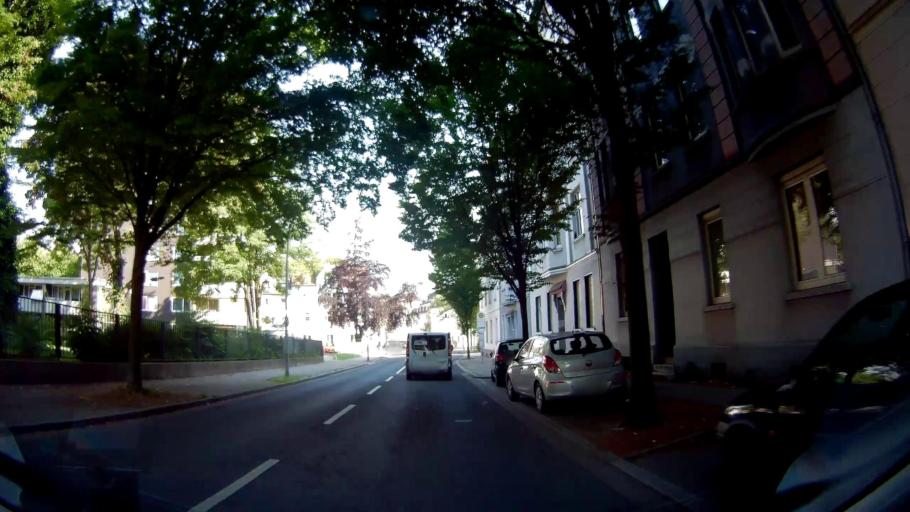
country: DE
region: North Rhine-Westphalia
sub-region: Regierungsbezirk Arnsberg
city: Herne
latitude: 51.5390
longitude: 7.2284
